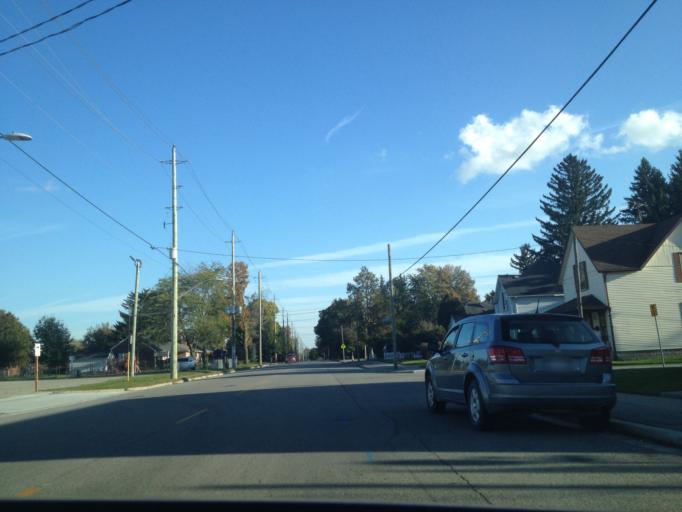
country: CA
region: Ontario
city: Delaware
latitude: 42.6006
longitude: -81.6027
